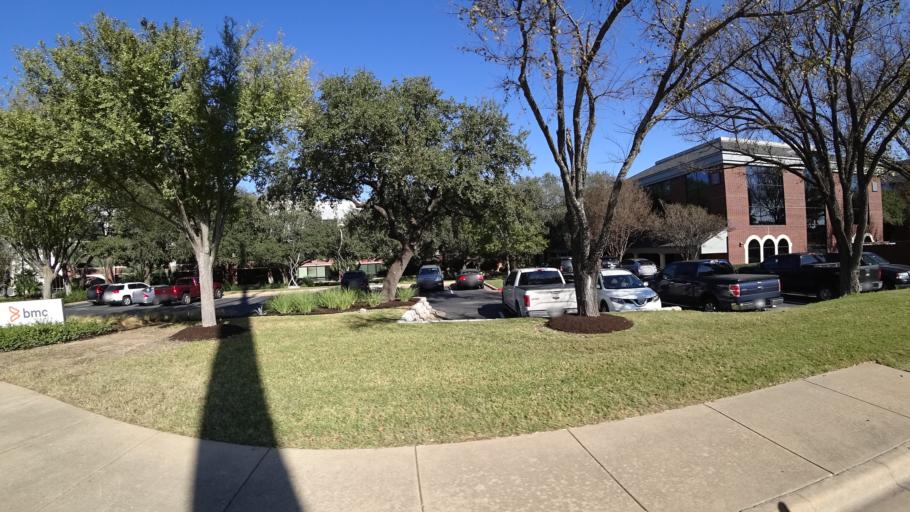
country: US
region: Texas
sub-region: Williamson County
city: Jollyville
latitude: 30.4008
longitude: -97.7506
